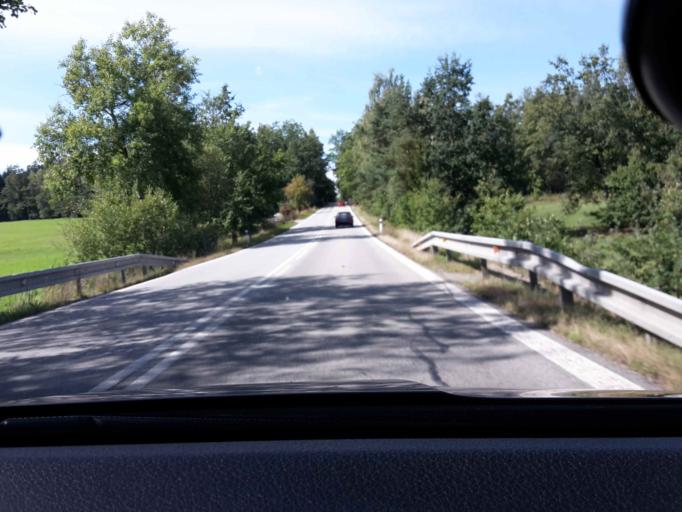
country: CZ
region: Jihocesky
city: Kardasova Recice
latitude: 49.1746
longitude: 14.8912
